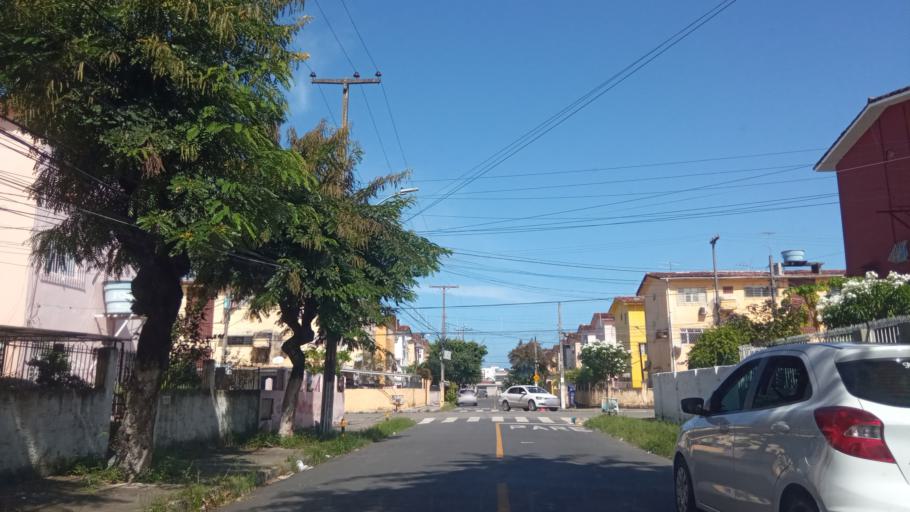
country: BR
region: Pernambuco
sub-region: Recife
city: Recife
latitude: -8.1147
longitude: -34.9224
